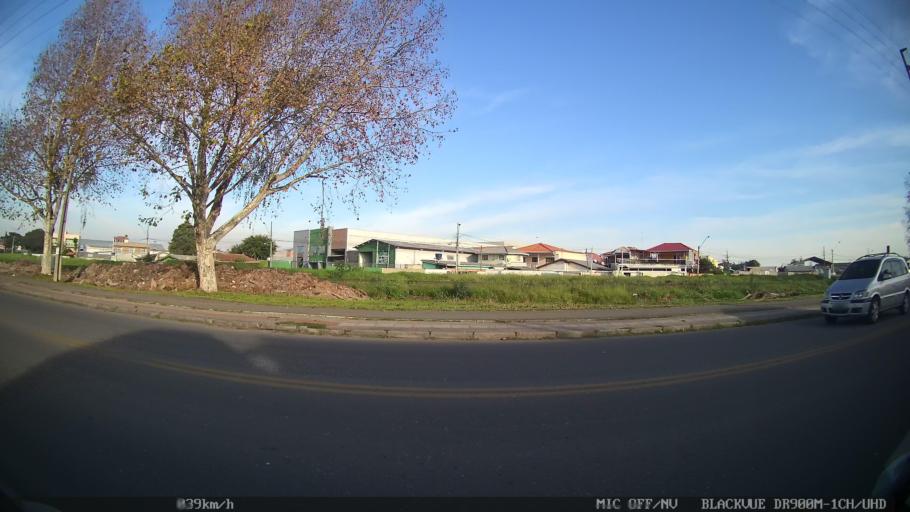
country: BR
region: Parana
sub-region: Pinhais
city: Pinhais
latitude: -25.4399
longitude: -49.1787
